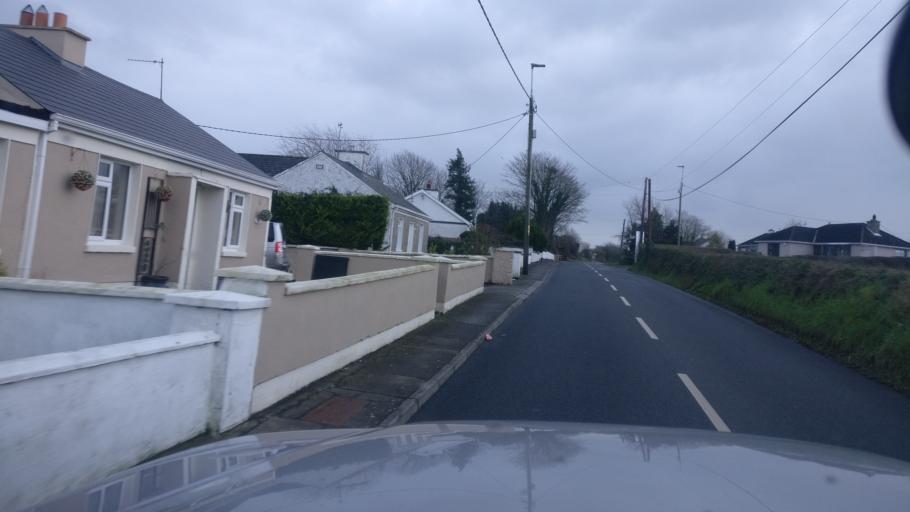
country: IE
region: Munster
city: Nenagh Bridge
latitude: 52.9922
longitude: -8.1215
